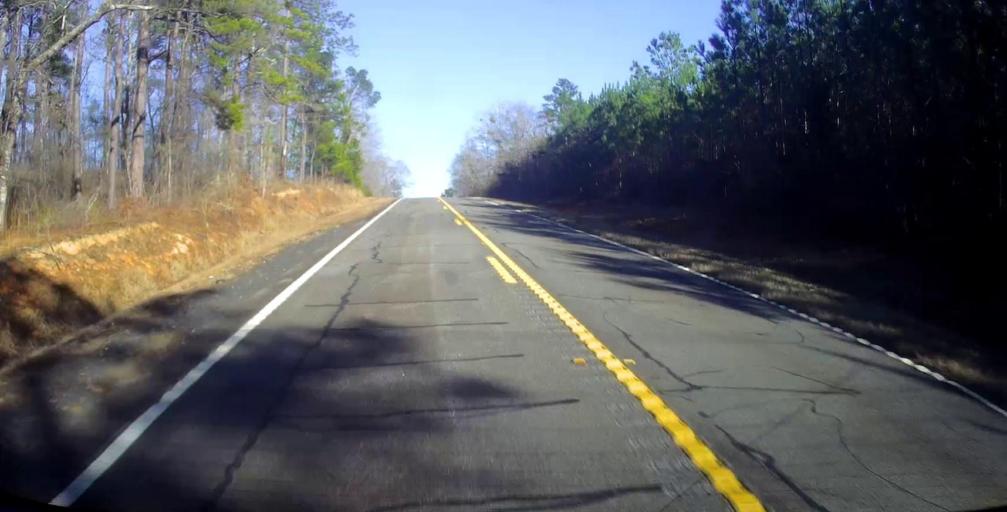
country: US
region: Georgia
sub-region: Talbot County
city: Talbotton
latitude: 32.6724
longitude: -84.5012
